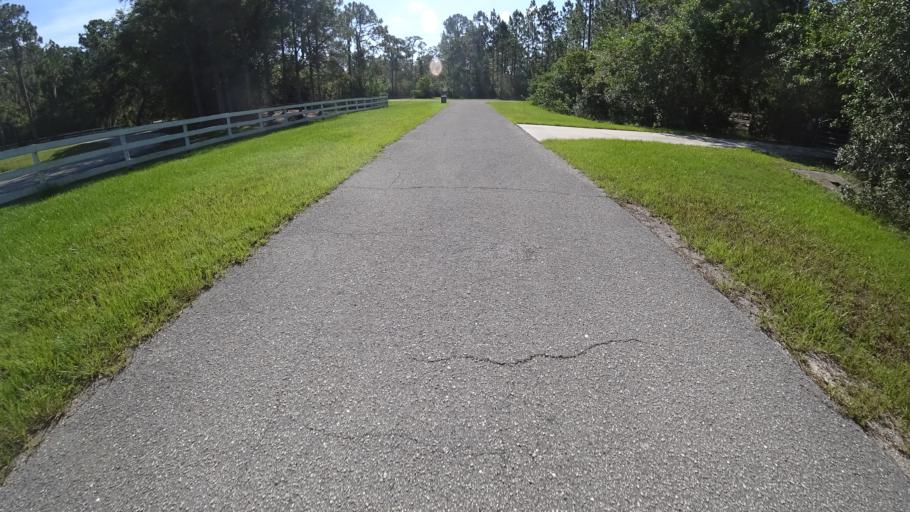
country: US
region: Florida
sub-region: Sarasota County
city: The Meadows
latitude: 27.4261
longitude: -82.3424
